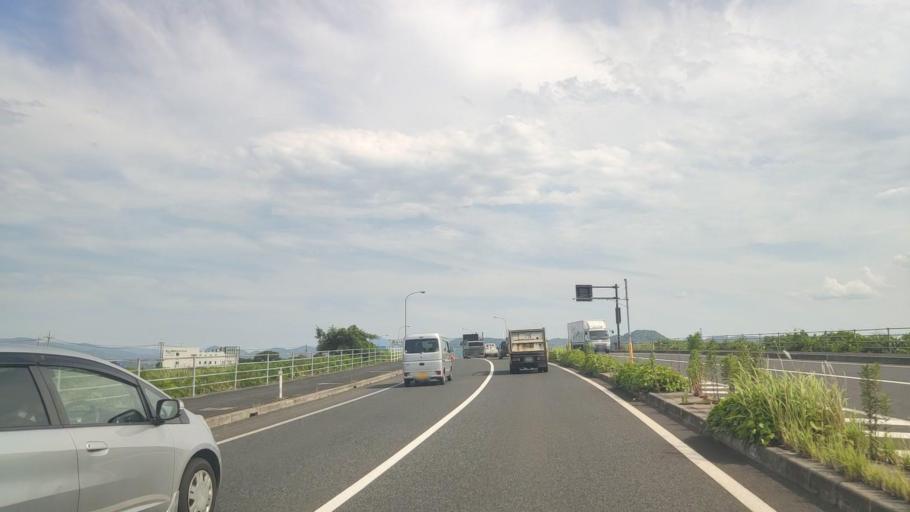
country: JP
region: Tottori
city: Tottori
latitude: 35.4820
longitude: 134.2061
